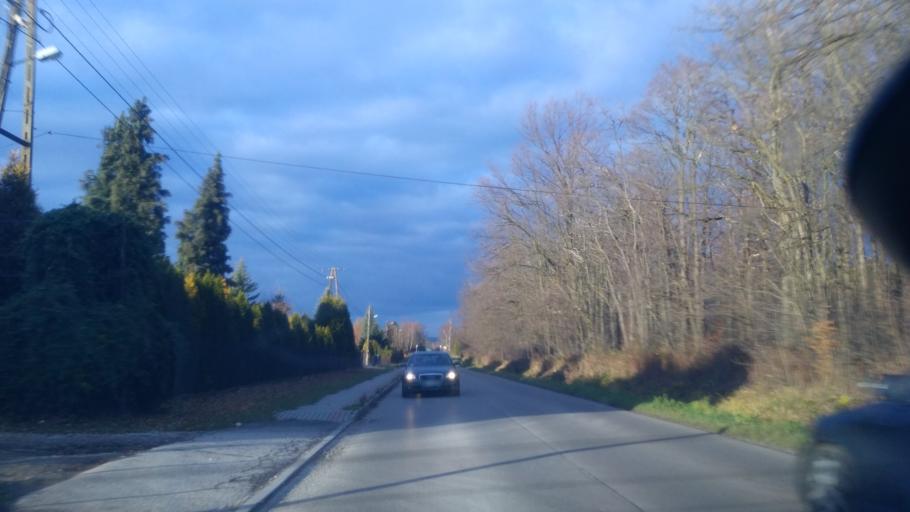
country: PL
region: Subcarpathian Voivodeship
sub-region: Powiat rzeszowski
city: Krasne
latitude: 50.0501
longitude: 22.1224
